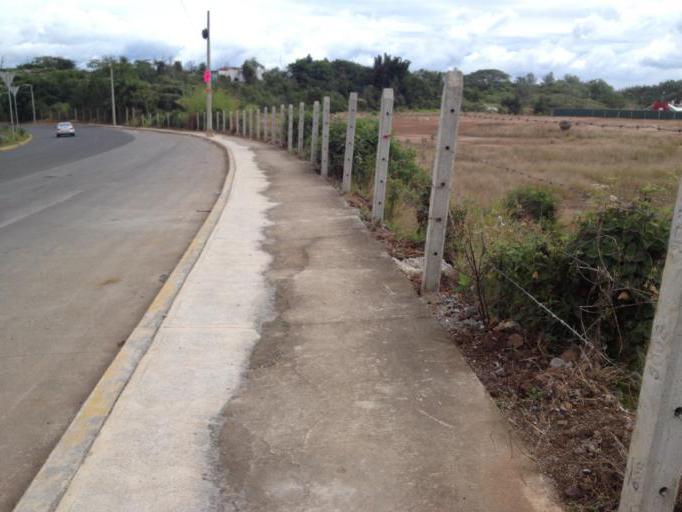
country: MX
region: Veracruz
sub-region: Emiliano Zapata
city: Las Trancas
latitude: 19.5050
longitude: -96.8573
